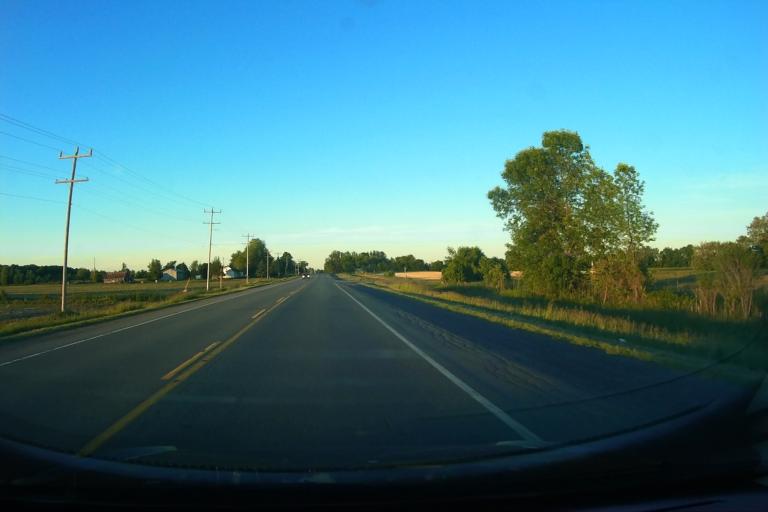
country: CA
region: Ontario
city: Casselman
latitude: 45.0951
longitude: -75.2769
